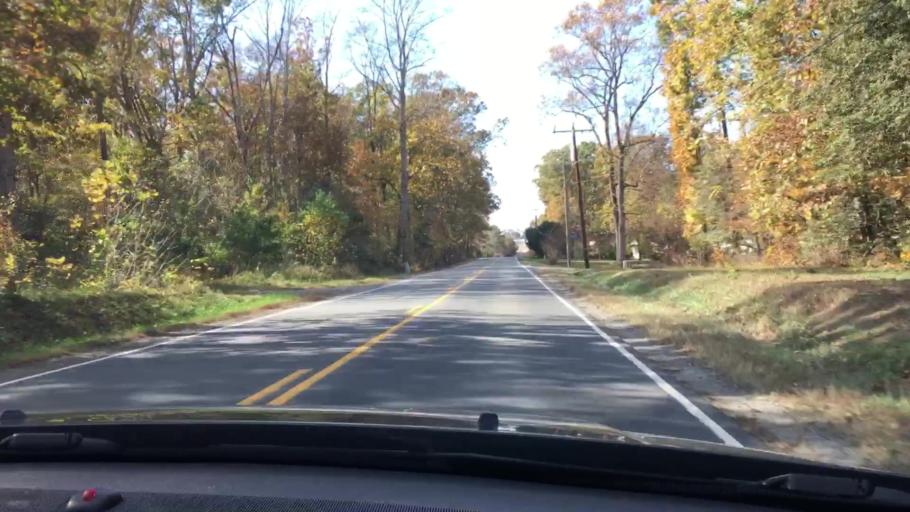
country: US
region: Virginia
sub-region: King and Queen County
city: King and Queen Court House
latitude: 37.5911
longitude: -76.8766
